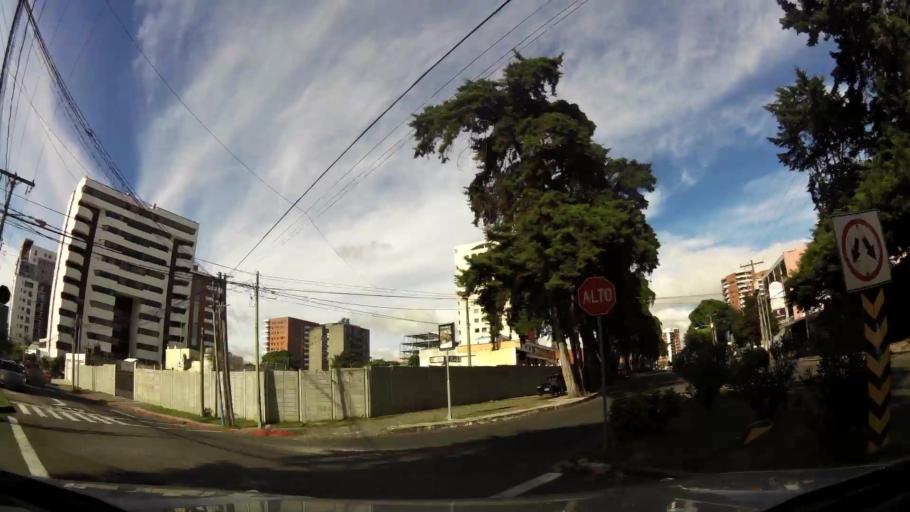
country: GT
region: Guatemala
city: Santa Catarina Pinula
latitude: 14.5850
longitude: -90.5172
